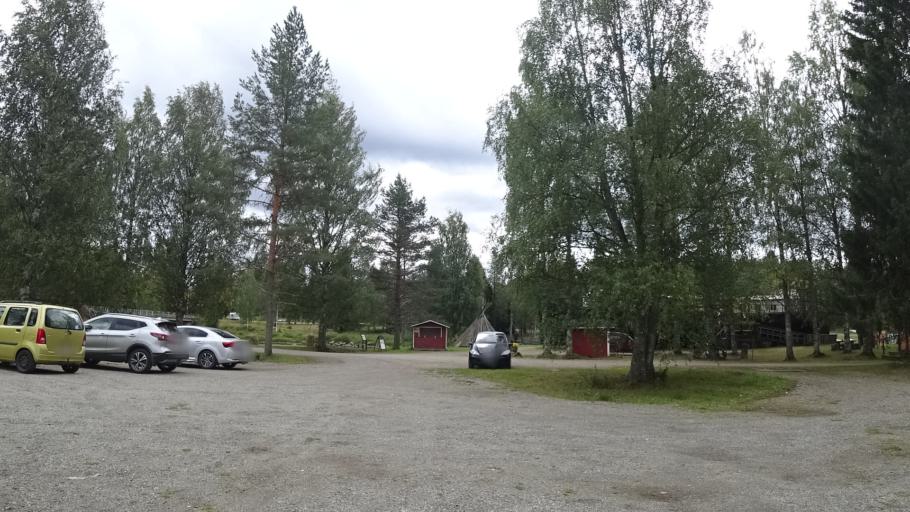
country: FI
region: North Karelia
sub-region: Joensuu
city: Ilomantsi
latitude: 62.6413
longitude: 31.2854
